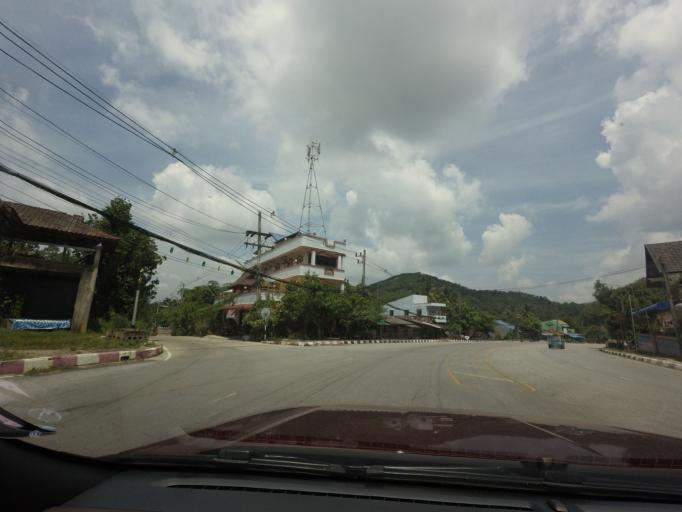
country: TH
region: Yala
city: Betong
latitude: 5.7689
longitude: 101.0598
